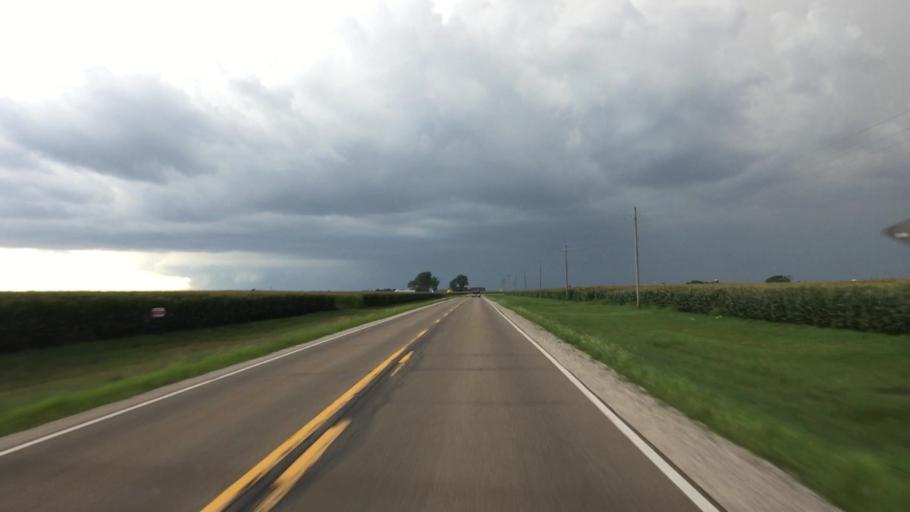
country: US
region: Iowa
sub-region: Henry County
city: New London
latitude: 40.7732
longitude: -91.4669
